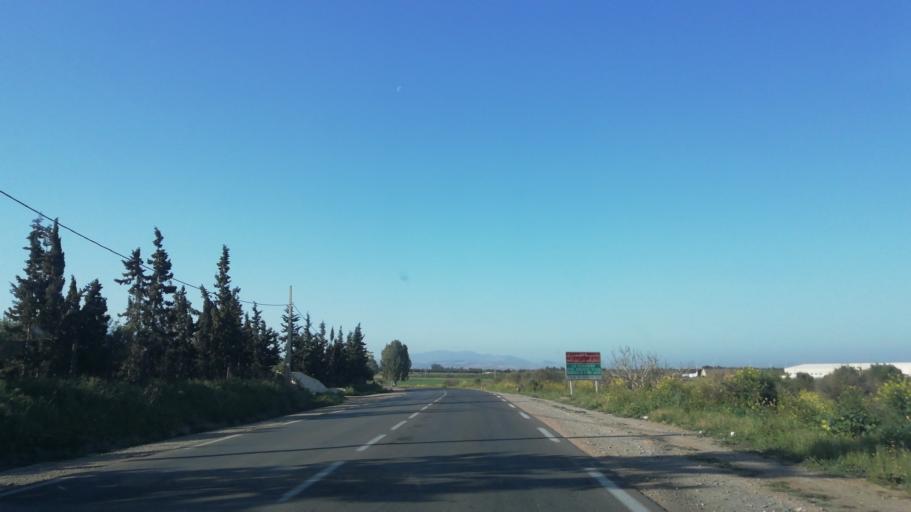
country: DZ
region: Mascara
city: Mascara
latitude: 35.6363
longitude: 0.1354
